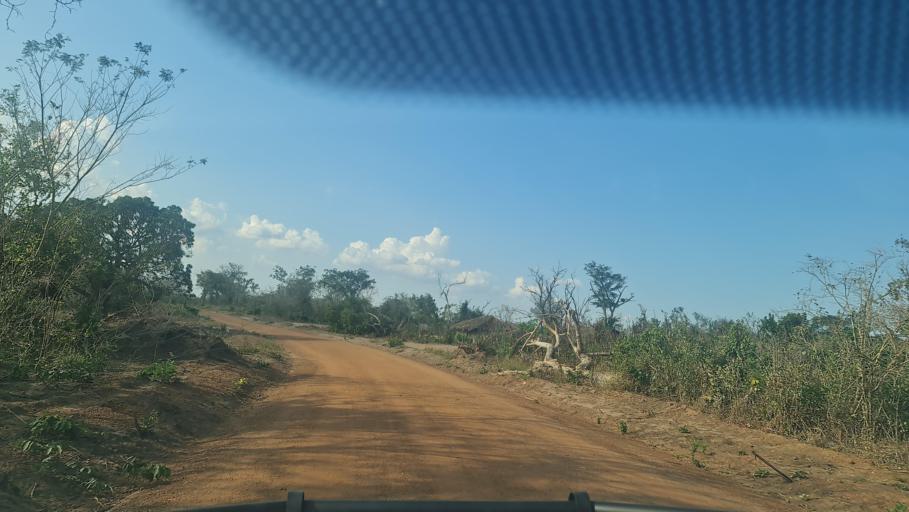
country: MZ
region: Nampula
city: Ilha de Mocambique
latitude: -15.5146
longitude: 40.1640
